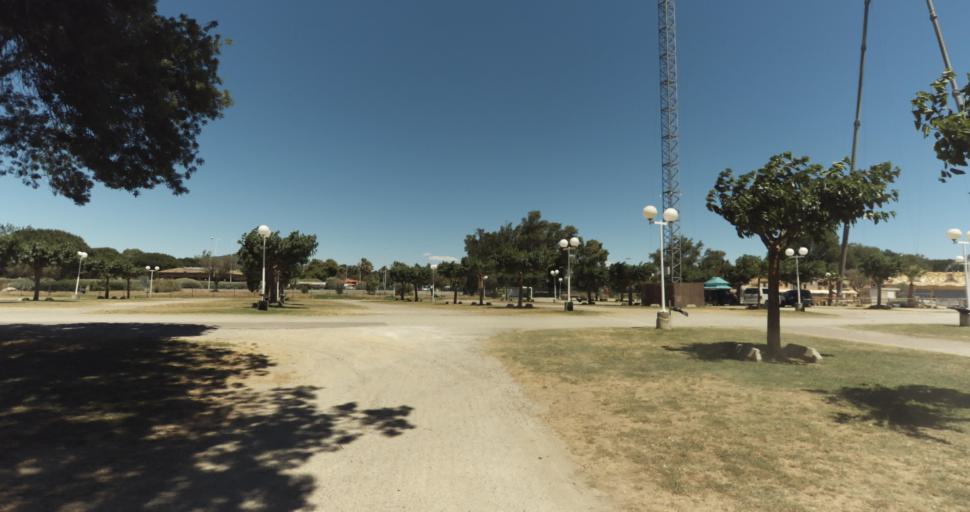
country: FR
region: Provence-Alpes-Cote d'Azur
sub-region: Departement du Var
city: Gassin
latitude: 43.2605
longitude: 6.5772
